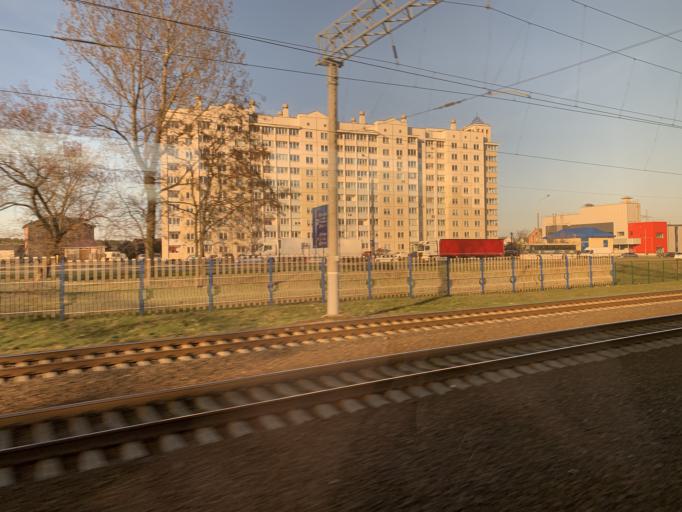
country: BY
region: Minsk
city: Zhdanovichy
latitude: 53.9462
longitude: 27.4295
